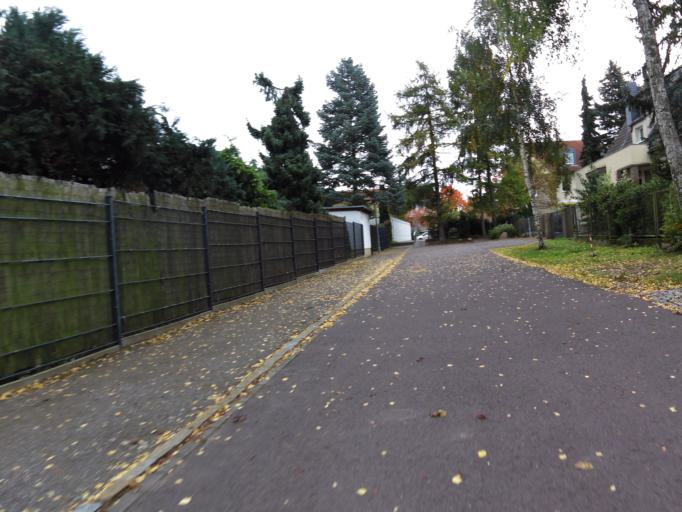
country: DE
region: Saxony
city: Grossposna
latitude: 51.3124
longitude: 12.4534
